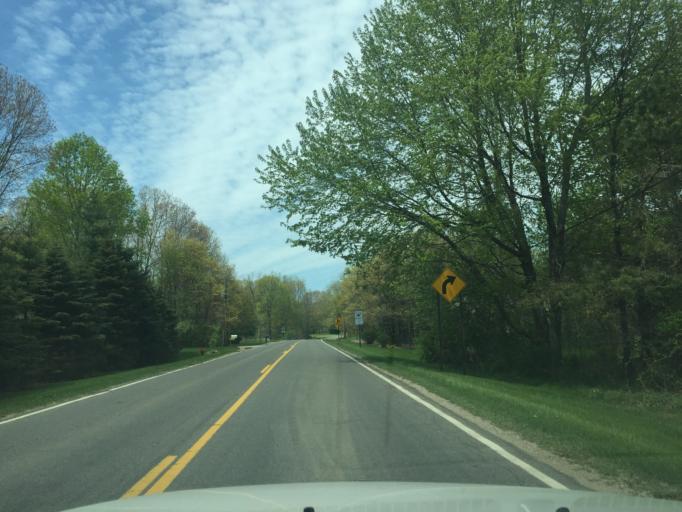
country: US
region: Michigan
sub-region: Berrien County
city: Stevensville
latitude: 41.9987
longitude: -86.5144
